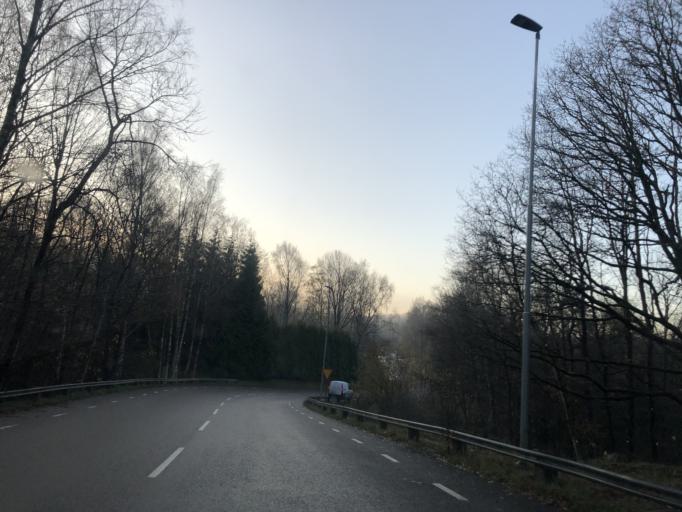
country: SE
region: Vaestra Goetaland
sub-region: Goteborg
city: Hammarkullen
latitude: 57.7920
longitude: 12.0315
